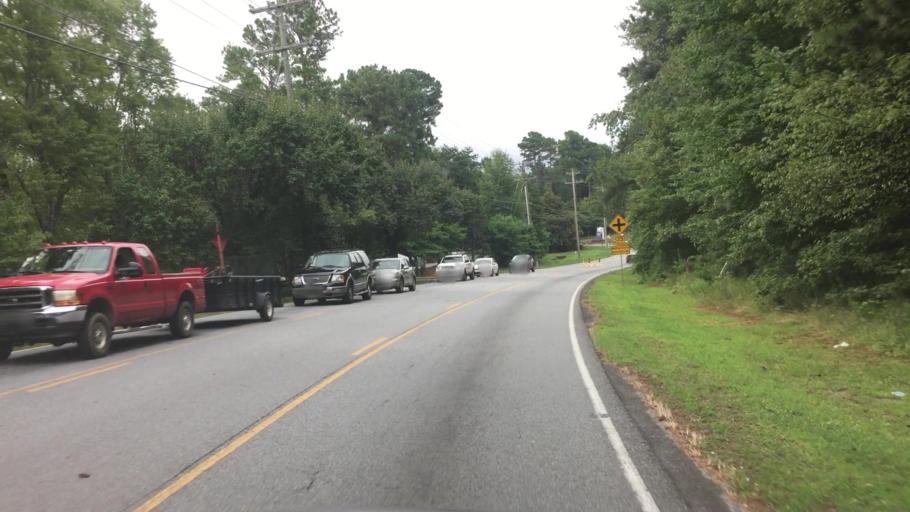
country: US
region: Georgia
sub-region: Fulton County
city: Johns Creek
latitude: 34.0981
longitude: -84.2123
